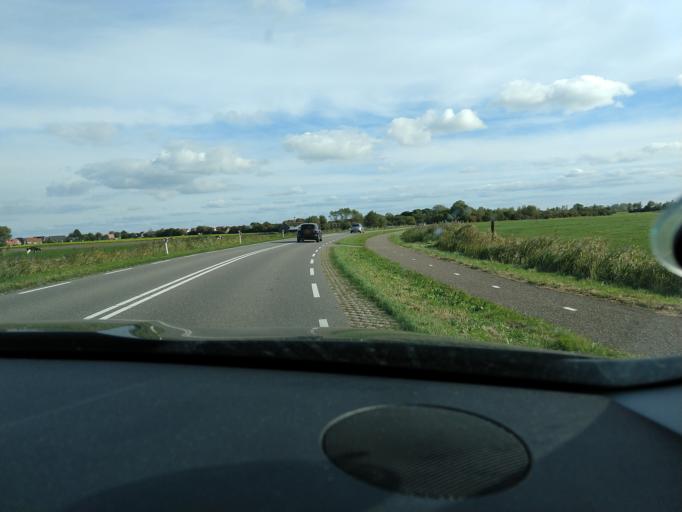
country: NL
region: Zeeland
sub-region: Gemeente Middelburg
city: Middelburg
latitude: 51.5368
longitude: 3.5510
